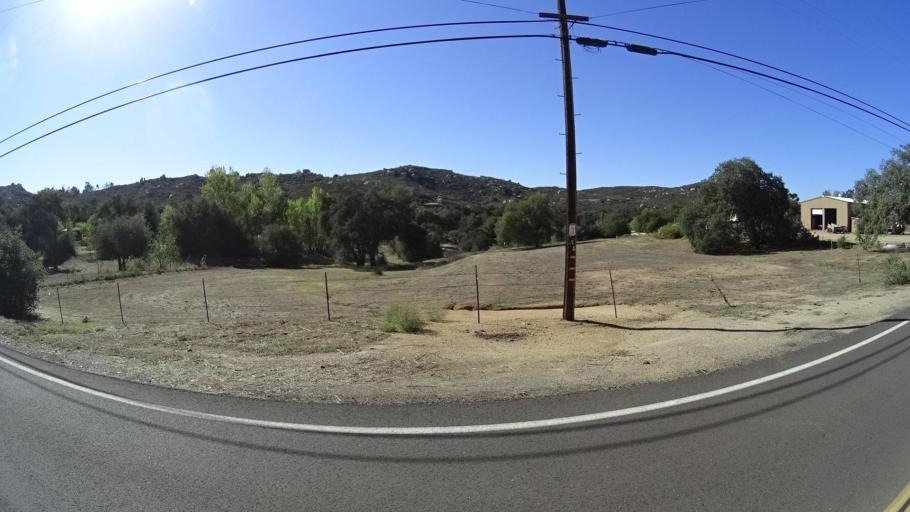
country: MX
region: Baja California
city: Tecate
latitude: 32.6763
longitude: -116.7251
